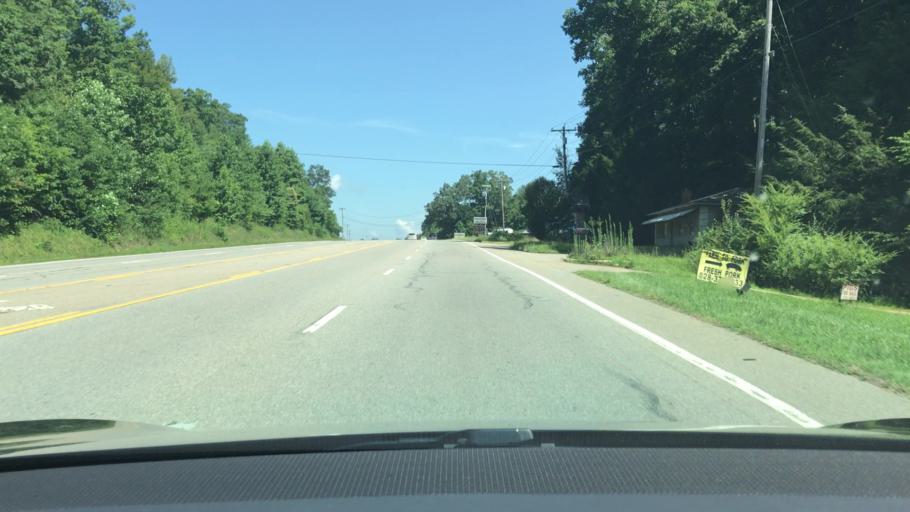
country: US
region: North Carolina
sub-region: Macon County
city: Franklin
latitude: 35.1028
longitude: -83.3857
